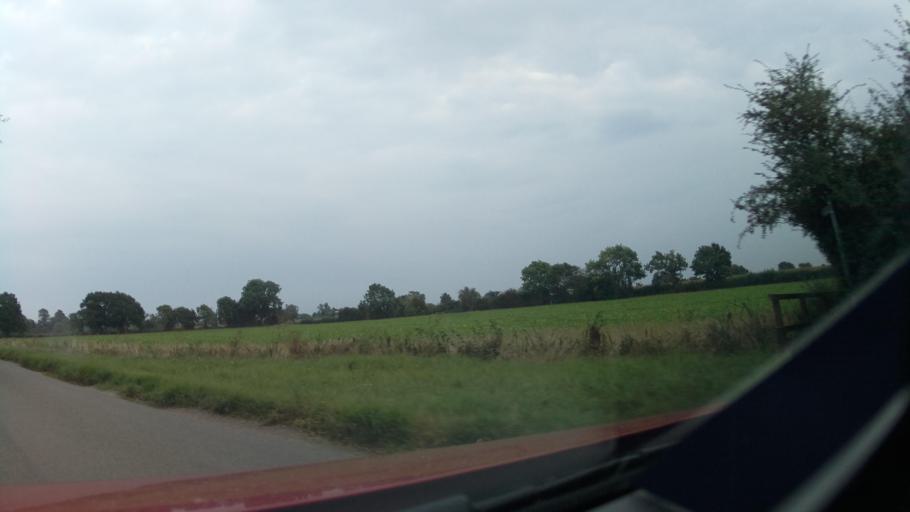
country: GB
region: England
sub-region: Lincolnshire
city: Skellingthorpe
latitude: 53.1430
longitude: -0.6557
